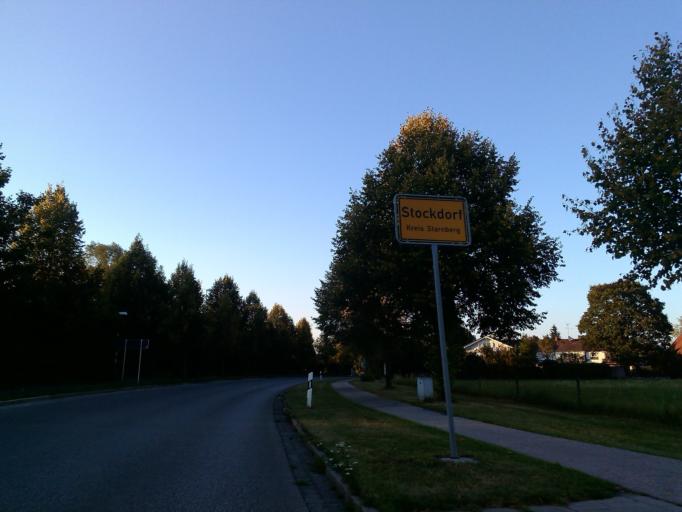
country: DE
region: Bavaria
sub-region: Upper Bavaria
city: Krailling
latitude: 48.0821
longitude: 11.3986
